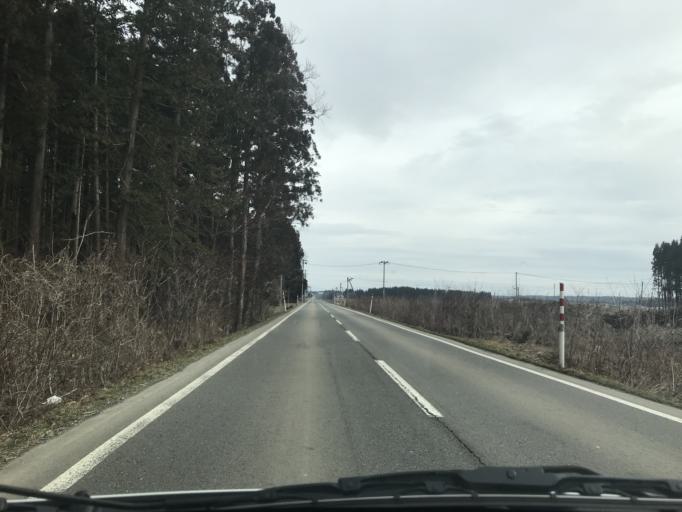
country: JP
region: Iwate
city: Kitakami
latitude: 39.3143
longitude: 141.0196
